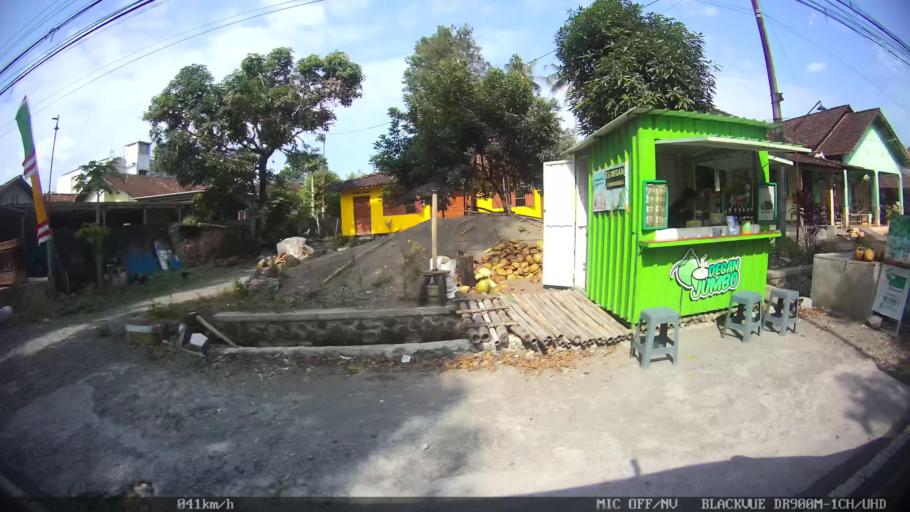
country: ID
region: Daerah Istimewa Yogyakarta
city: Depok
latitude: -7.7320
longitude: 110.4349
